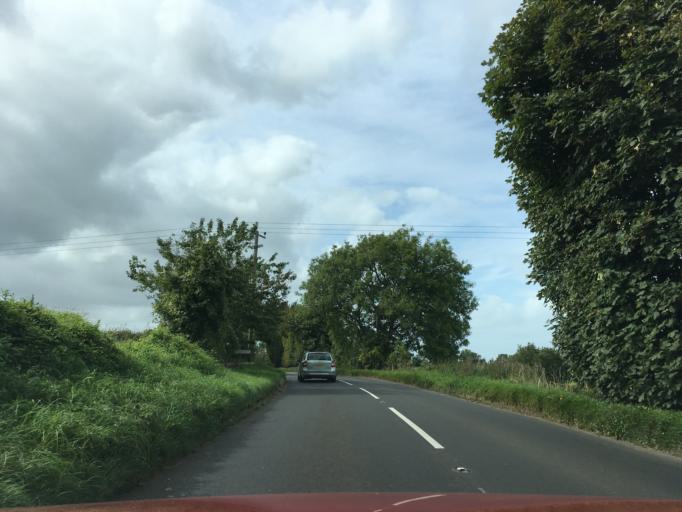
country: GB
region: England
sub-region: Gloucestershire
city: Stonehouse
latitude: 51.6906
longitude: -2.2796
